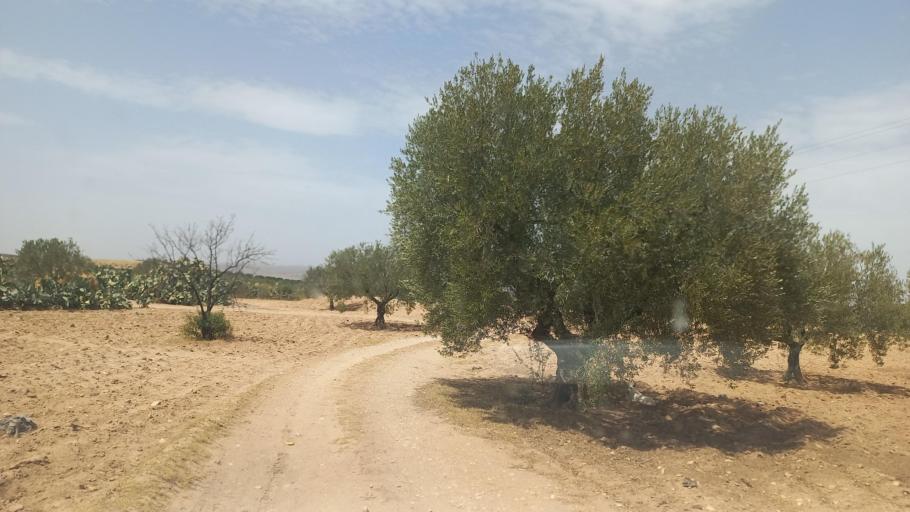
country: TN
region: Al Qasrayn
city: Kasserine
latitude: 35.2654
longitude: 8.9847
